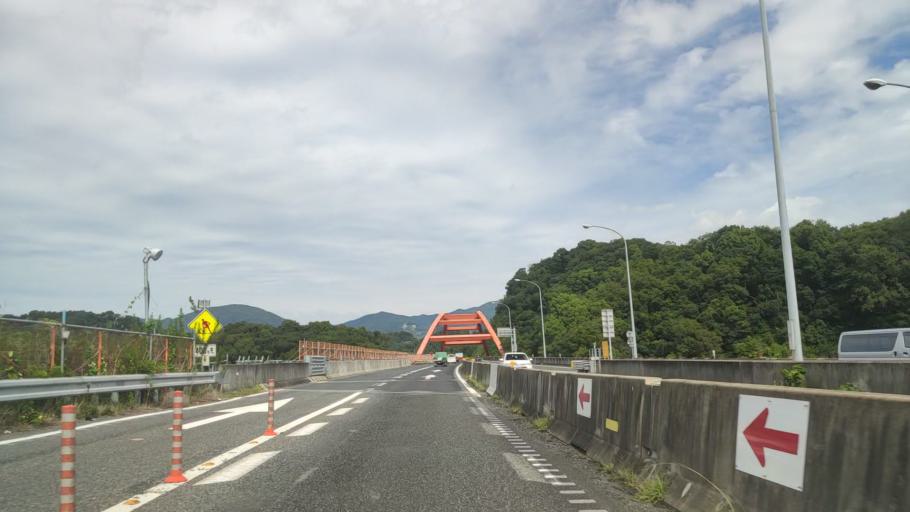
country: JP
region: Wakayama
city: Kainan
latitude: 34.0380
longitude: 135.2015
